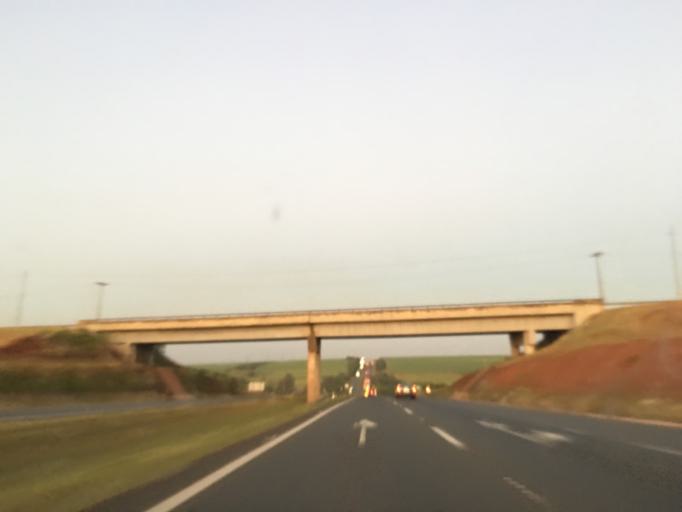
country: BR
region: Sao Paulo
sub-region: Piracicaba
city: Piracicaba
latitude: -22.7239
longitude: -47.5855
